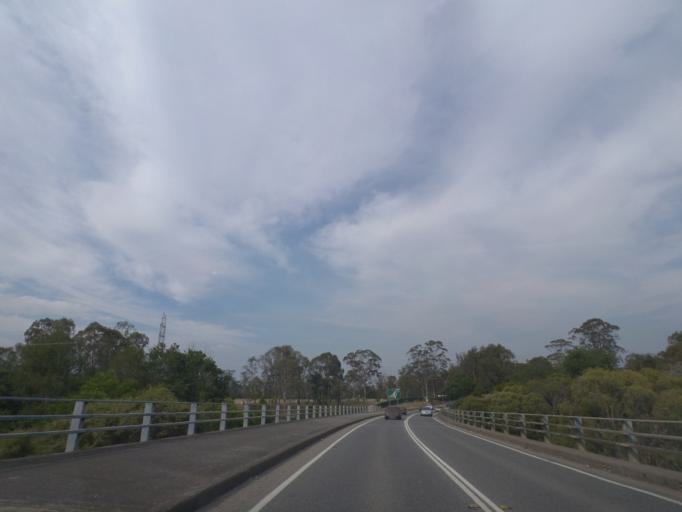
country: AU
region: Queensland
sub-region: Brisbane
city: Sunnybank
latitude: -27.5969
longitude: 153.0156
